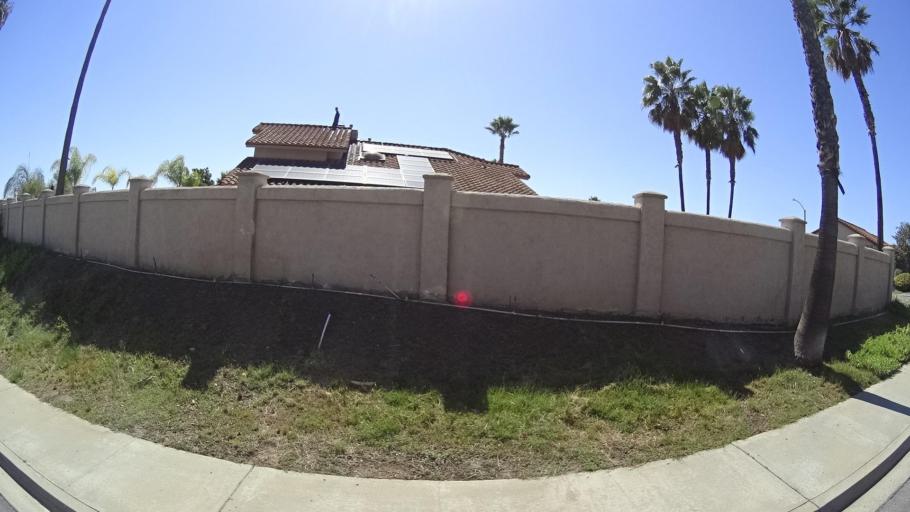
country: US
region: California
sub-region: San Diego County
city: Rancho San Diego
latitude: 32.7572
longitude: -116.9385
